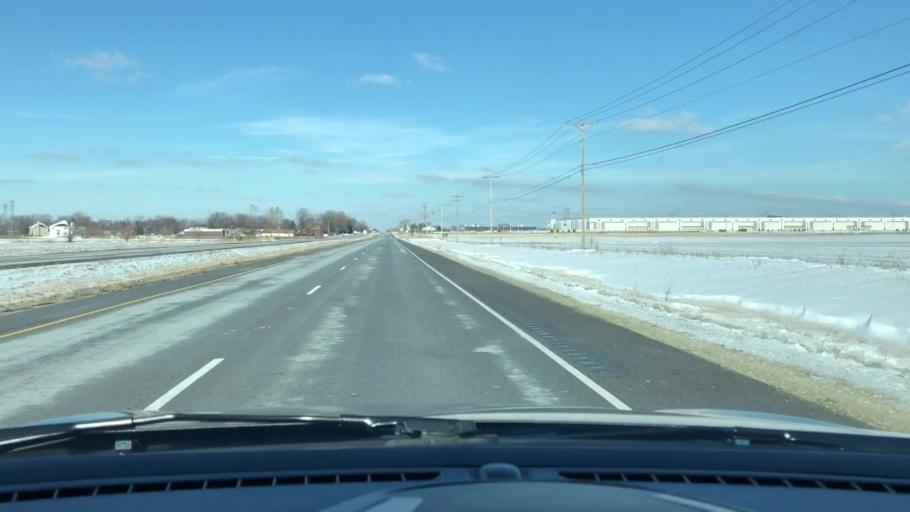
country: US
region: Illinois
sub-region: Will County
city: Preston Heights
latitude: 41.4418
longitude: -88.0788
